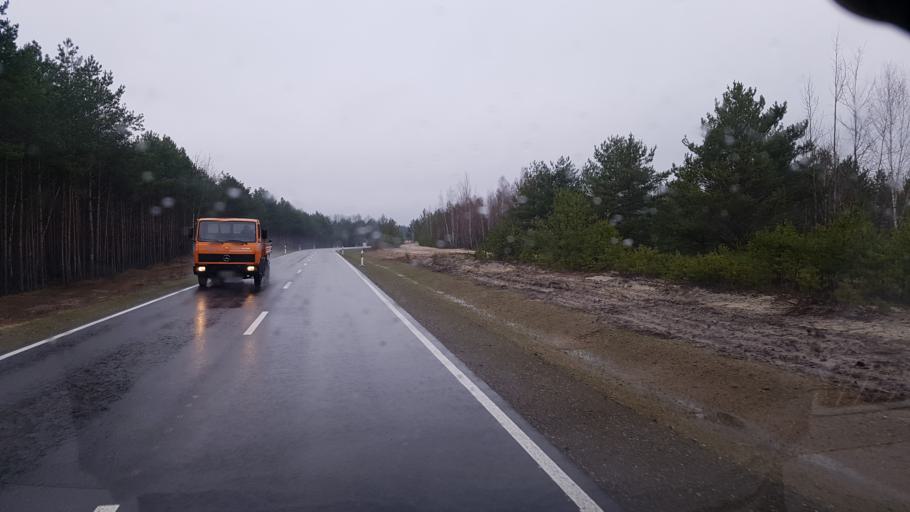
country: DE
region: Brandenburg
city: Lauchhammer
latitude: 51.5316
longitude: 13.7747
